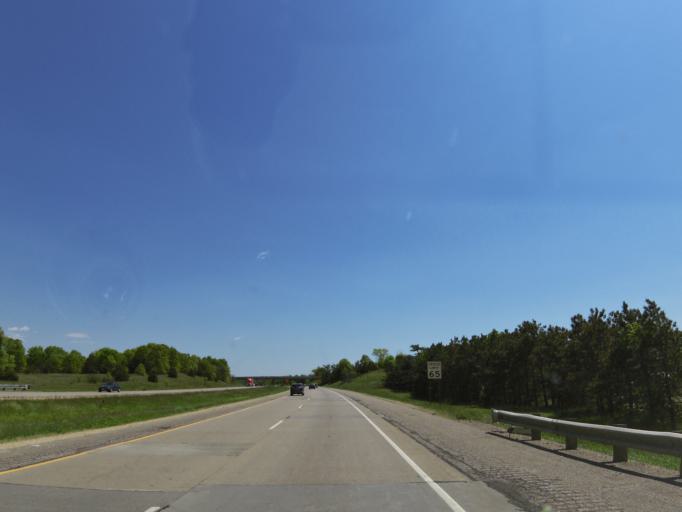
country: US
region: Wisconsin
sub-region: Juneau County
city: Mauston
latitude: 43.7868
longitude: -90.0475
